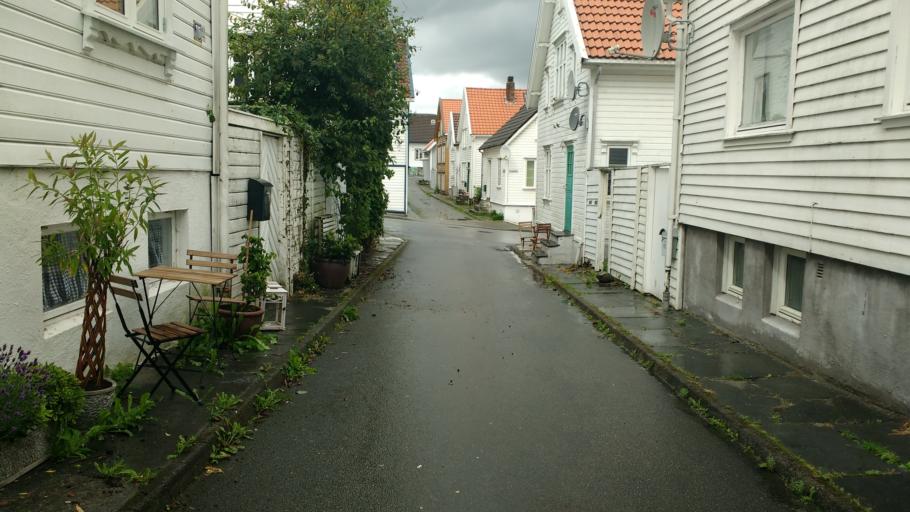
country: NO
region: Rogaland
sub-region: Stavanger
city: Stavanger
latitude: 58.9692
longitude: 5.7402
